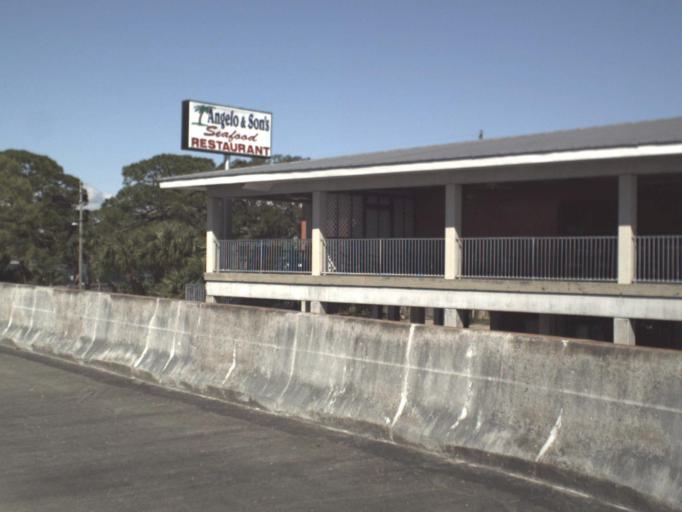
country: US
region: Florida
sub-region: Wakulla County
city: Crawfordville
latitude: 29.9768
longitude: -84.3832
